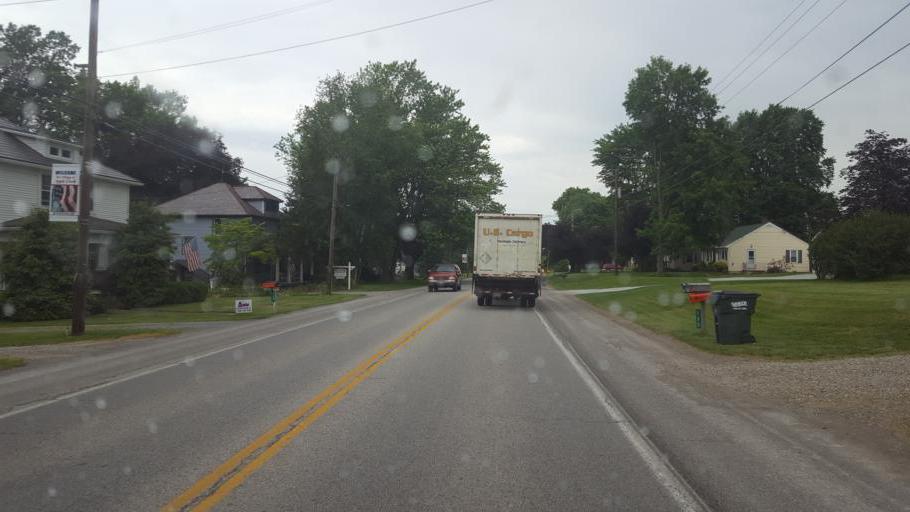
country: US
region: Ohio
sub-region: Wayne County
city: Apple Creek
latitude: 40.7421
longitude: -81.8267
